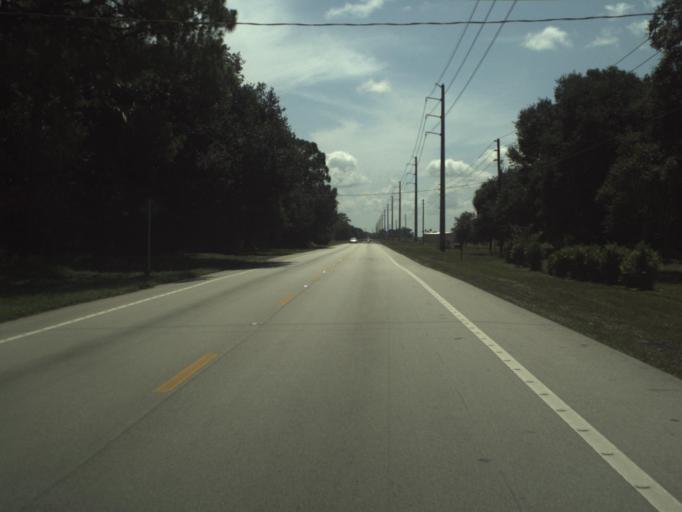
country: US
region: Florida
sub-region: Martin County
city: Indiantown
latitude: 27.0095
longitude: -80.4967
